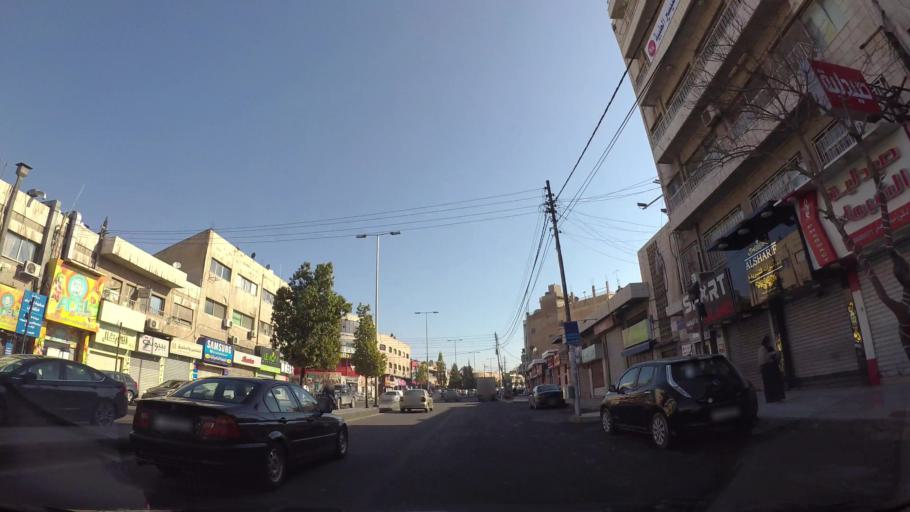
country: JO
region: Amman
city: Amman
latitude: 31.9807
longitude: 35.9860
